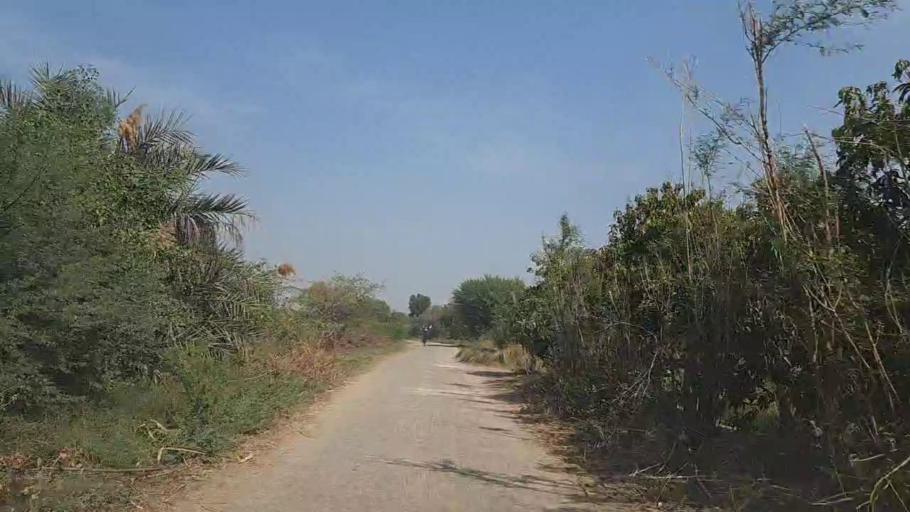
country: PK
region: Sindh
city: Mirpur Khas
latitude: 25.4926
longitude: 68.9208
